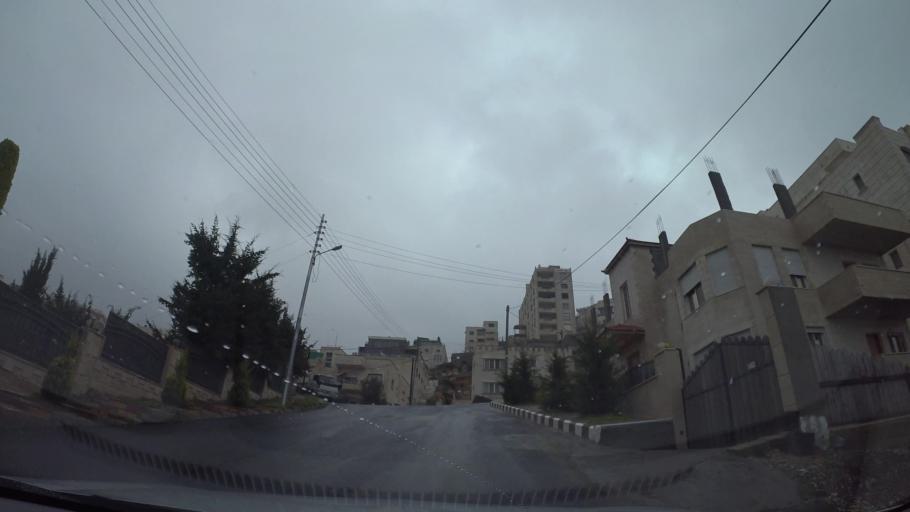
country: JO
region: Amman
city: Al Jubayhah
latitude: 32.0268
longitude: 35.8306
